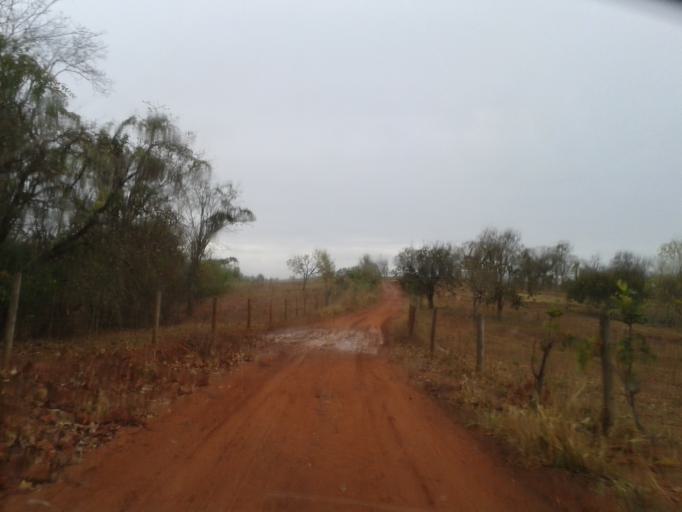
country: BR
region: Minas Gerais
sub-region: Campina Verde
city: Campina Verde
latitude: -19.3180
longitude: -49.5108
